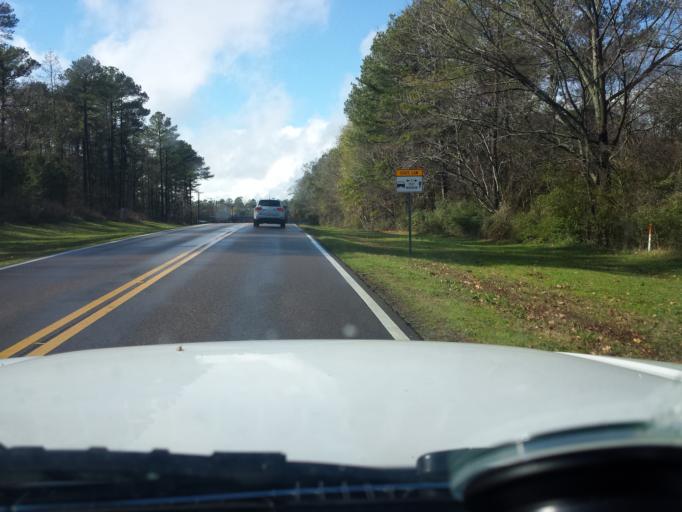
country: US
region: Mississippi
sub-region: Madison County
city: Ridgeland
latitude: 32.4215
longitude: -90.1025
